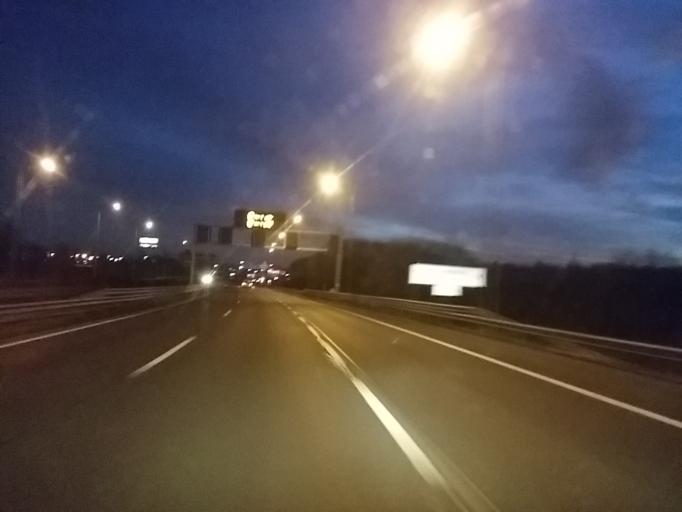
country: HU
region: Budapest
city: Budapest XV. keruelet
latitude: 47.6029
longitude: 19.1076
